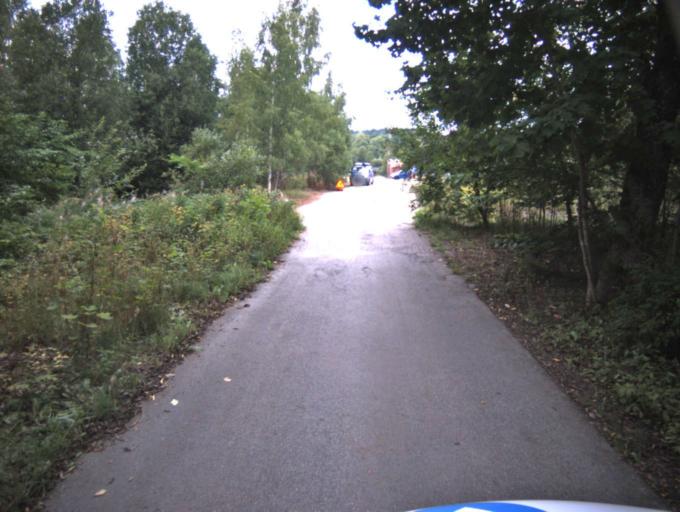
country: SE
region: Vaestra Goetaland
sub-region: Ulricehamns Kommun
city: Ulricehamn
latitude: 57.8413
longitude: 13.2915
